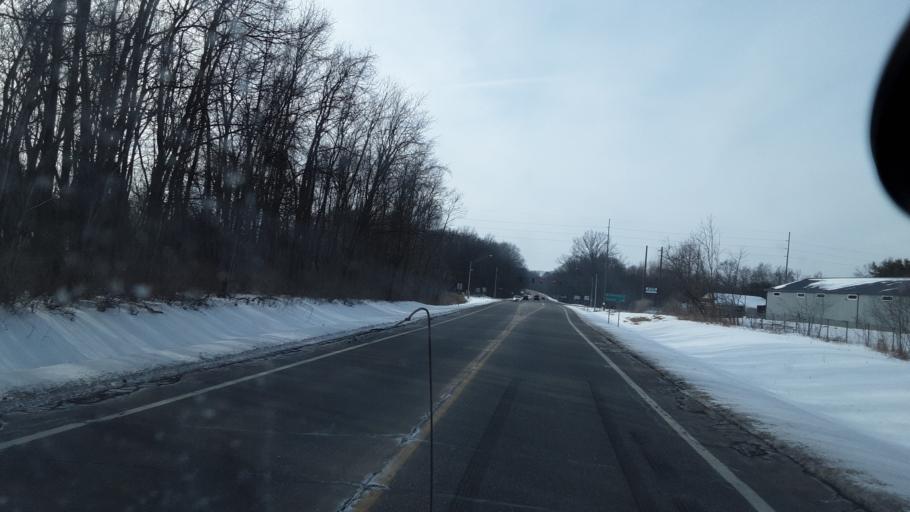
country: US
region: Ohio
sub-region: Summit County
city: Mogadore
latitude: 41.0287
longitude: -81.3908
